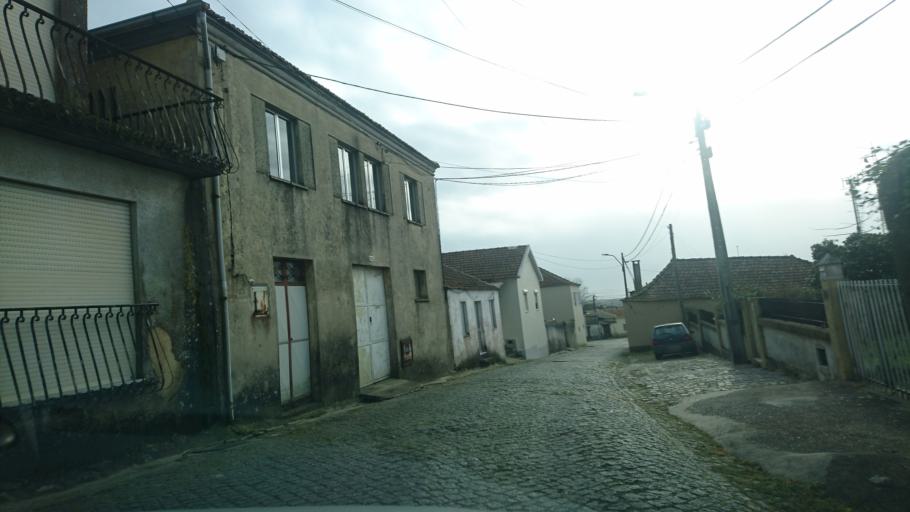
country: PT
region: Aveiro
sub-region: Ovar
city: Cortegaca
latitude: 40.9582
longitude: -8.6169
